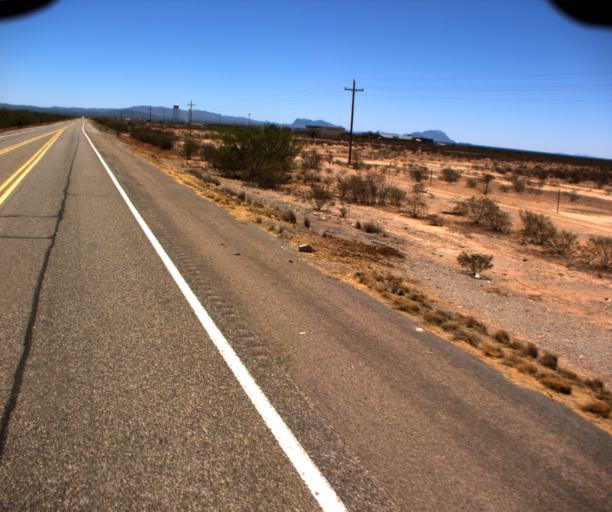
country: US
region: Arizona
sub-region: Pima County
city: Ajo
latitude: 32.1904
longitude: -112.4130
